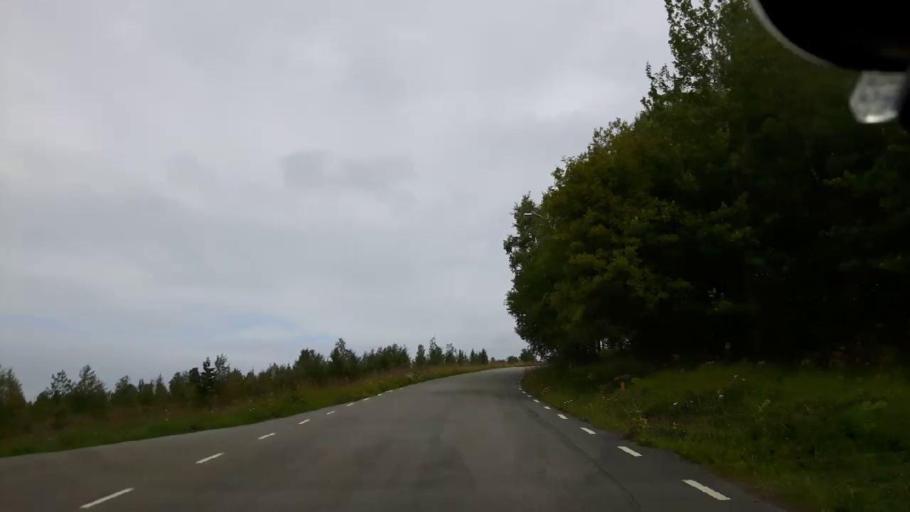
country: SE
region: Jaemtland
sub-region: OEstersunds Kommun
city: Ostersund
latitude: 63.1764
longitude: 14.5166
